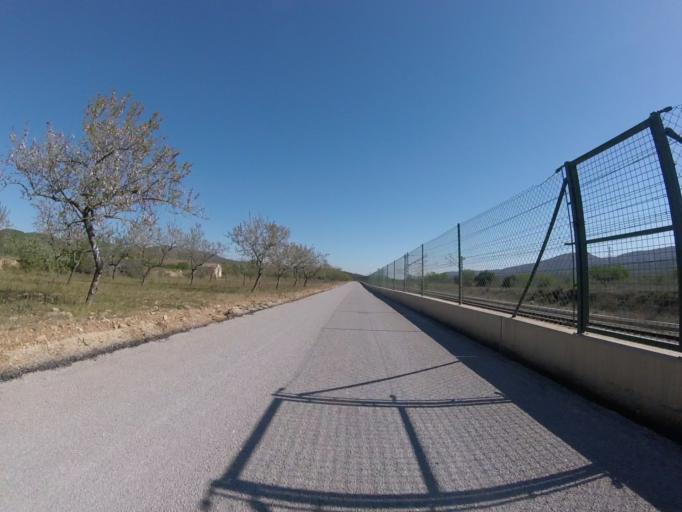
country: ES
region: Valencia
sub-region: Provincia de Castello
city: Alcala de Xivert
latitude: 40.3354
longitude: 0.2542
